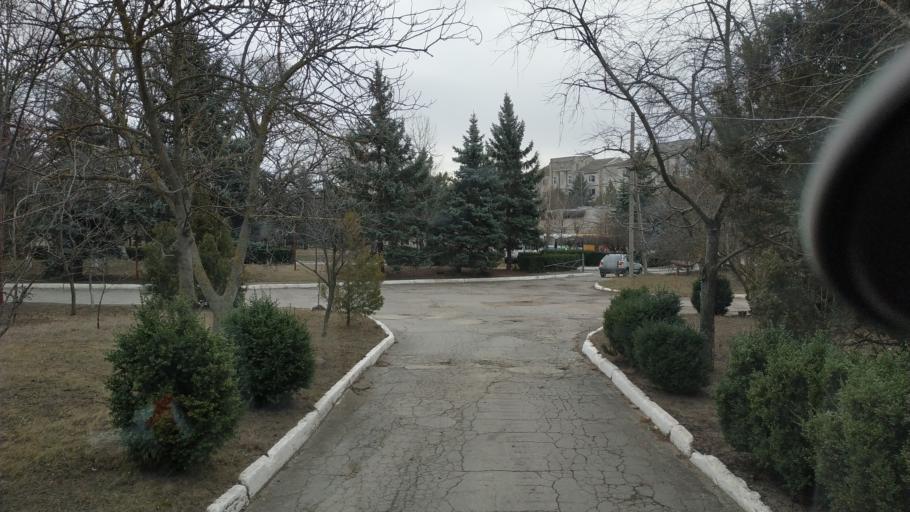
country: MD
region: Telenesti
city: Cocieri
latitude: 47.2920
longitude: 29.1194
